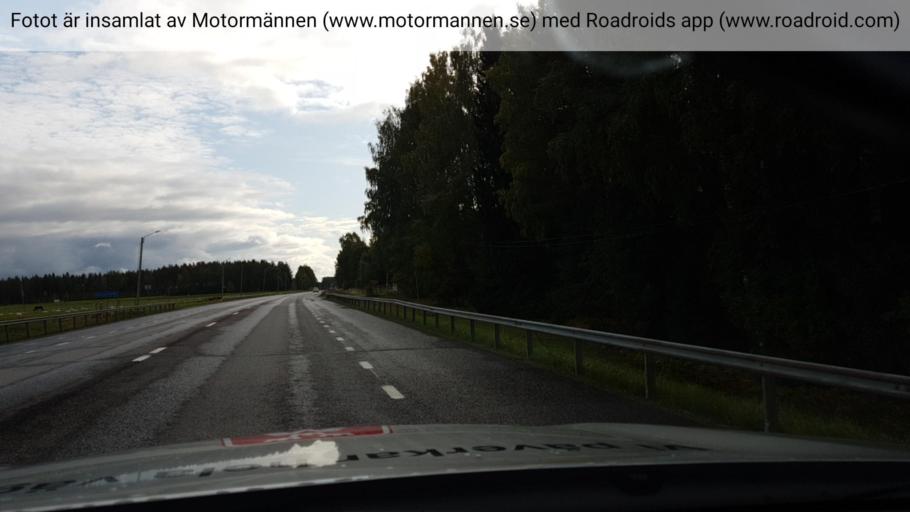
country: SE
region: Norrbotten
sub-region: Bodens Kommun
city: Saevast
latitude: 65.7253
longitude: 21.7859
